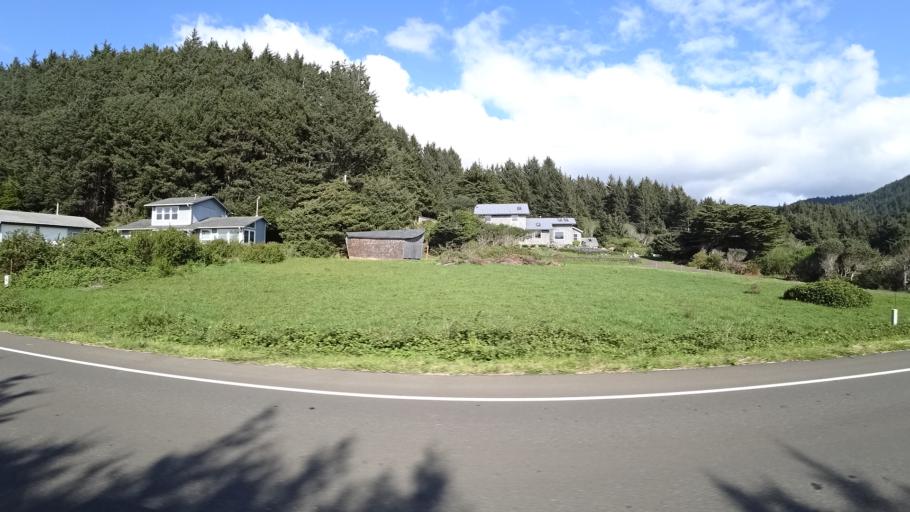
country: US
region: Oregon
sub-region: Lincoln County
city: Waldport
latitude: 44.2260
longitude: -124.1092
